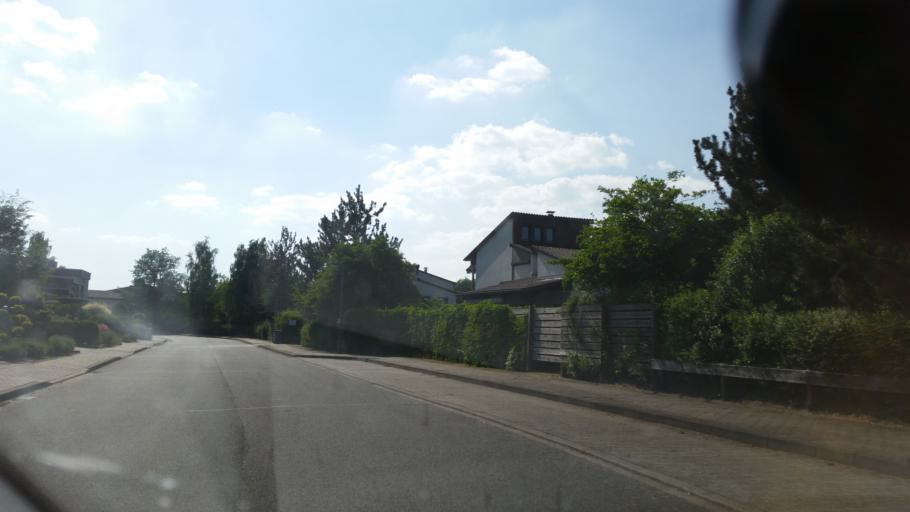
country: DE
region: Lower Saxony
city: Lehre
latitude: 52.3905
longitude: 10.7037
